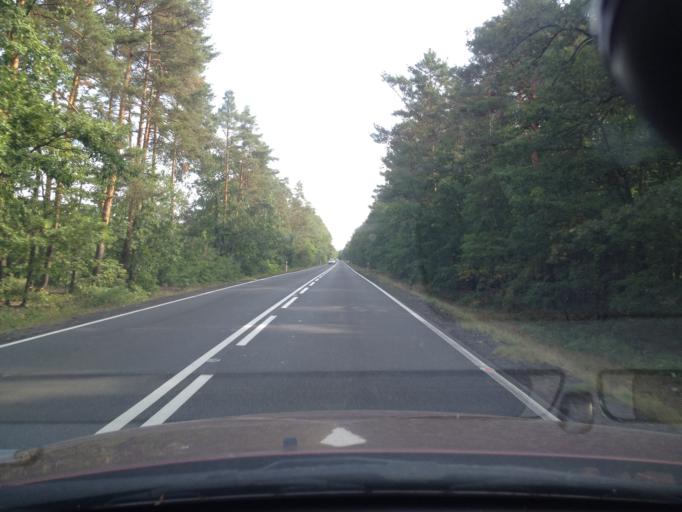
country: PL
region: Lubusz
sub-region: Powiat zaganski
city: Szprotawa
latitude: 51.4502
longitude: 15.6040
